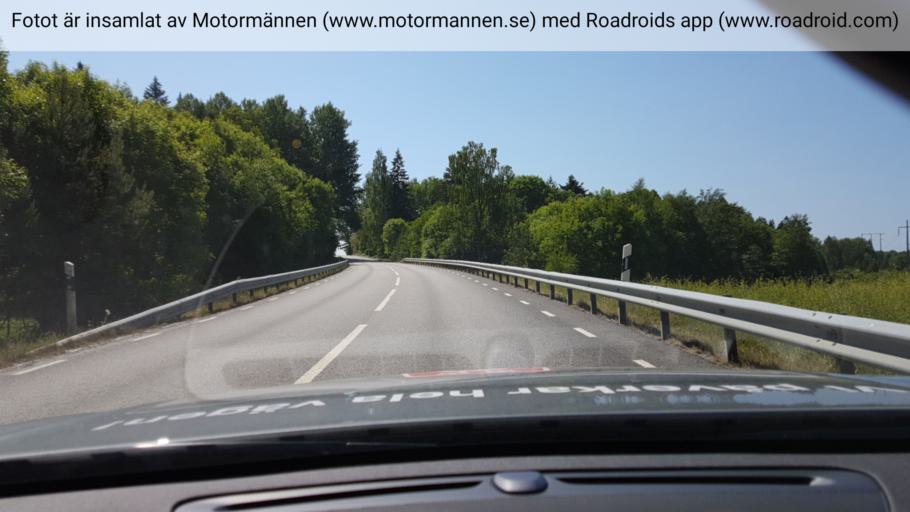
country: SE
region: Stockholm
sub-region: Norrtalje Kommun
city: Rimbo
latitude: 59.7535
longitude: 18.3876
